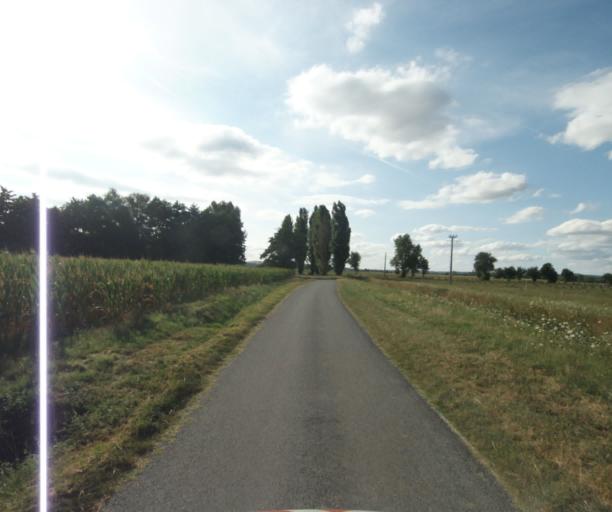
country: FR
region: Midi-Pyrenees
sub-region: Departement de la Haute-Garonne
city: Revel
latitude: 43.5060
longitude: 1.9902
